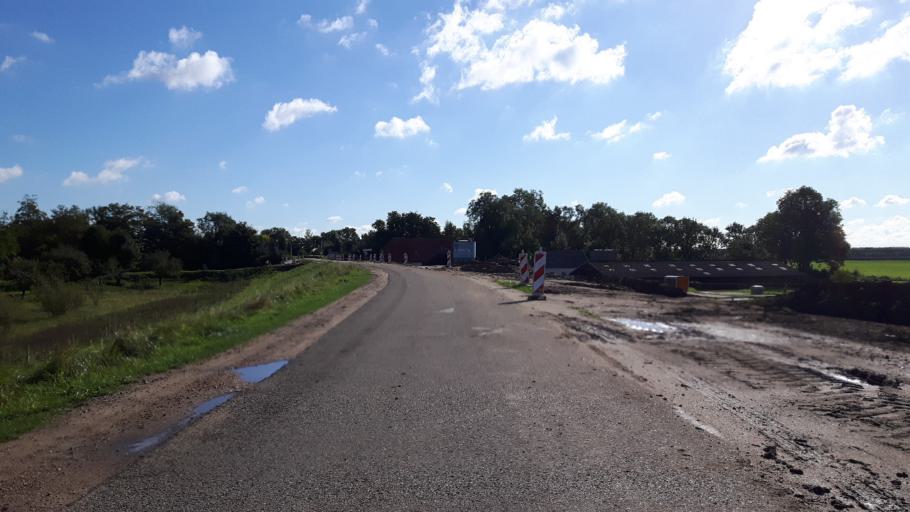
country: NL
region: Gelderland
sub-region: Gemeente Culemborg
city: Culemborg
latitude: 51.9595
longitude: 5.1867
